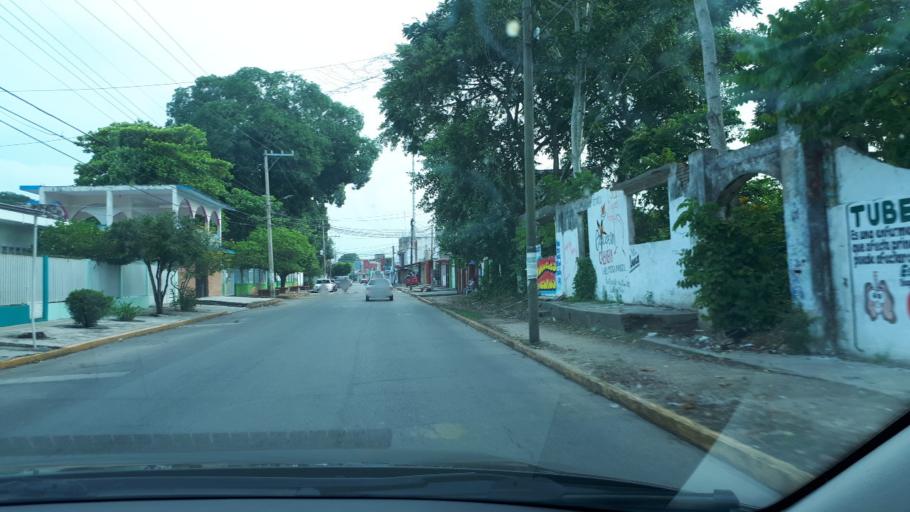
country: MX
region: Tabasco
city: Comalcalco
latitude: 18.2730
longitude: -93.2234
